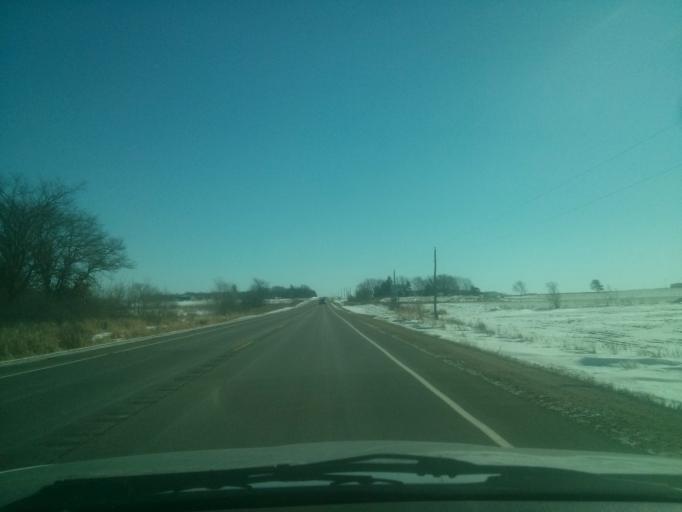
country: US
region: Wisconsin
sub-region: Polk County
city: Clear Lake
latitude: 45.1363
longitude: -92.3287
